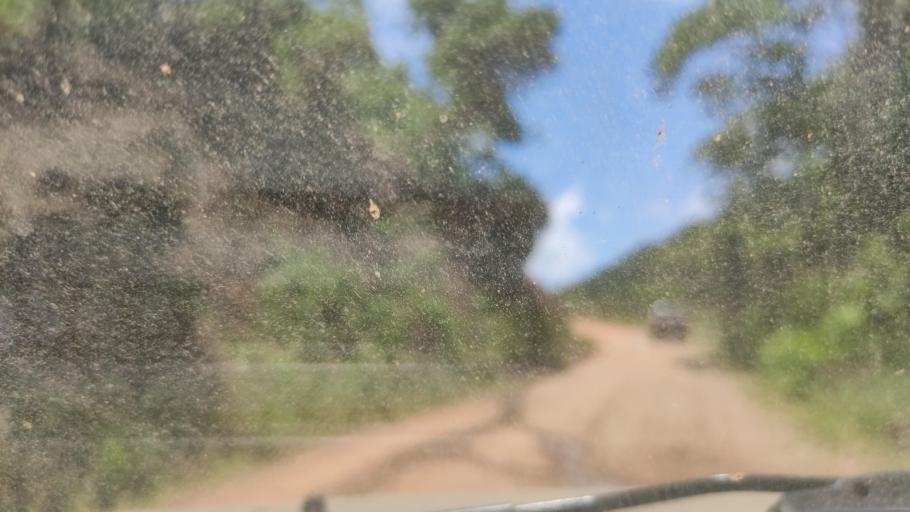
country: BR
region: Minas Gerais
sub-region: Cambui
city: Cambui
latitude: -22.6743
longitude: -45.9652
